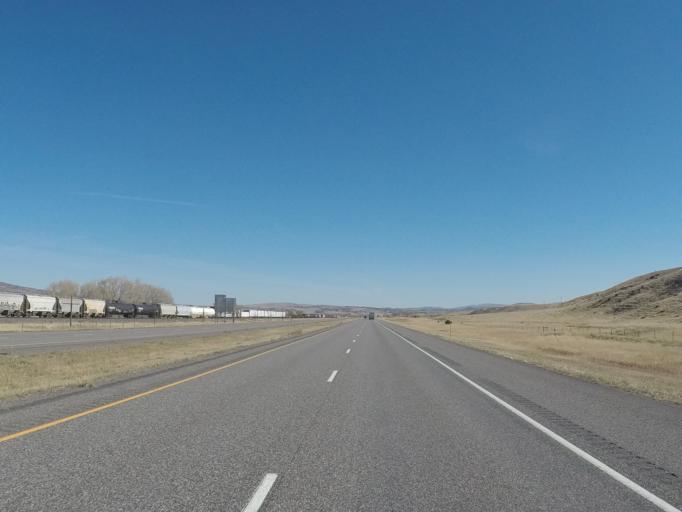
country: US
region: Montana
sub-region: Park County
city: Livingston
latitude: 45.7127
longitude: -110.4337
